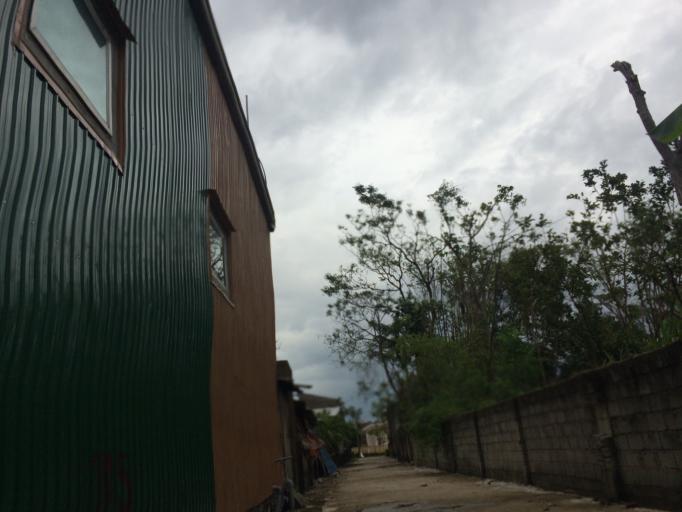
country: VN
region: Ha Tinh
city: Thach Ha
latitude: 18.3672
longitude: 105.8890
